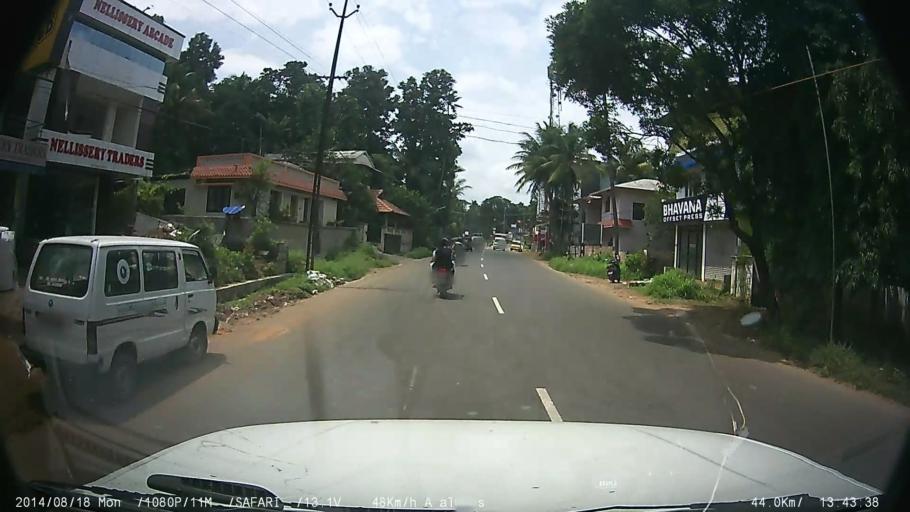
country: IN
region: Kerala
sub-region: Kottayam
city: Palackattumala
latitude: 9.6834
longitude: 76.5574
